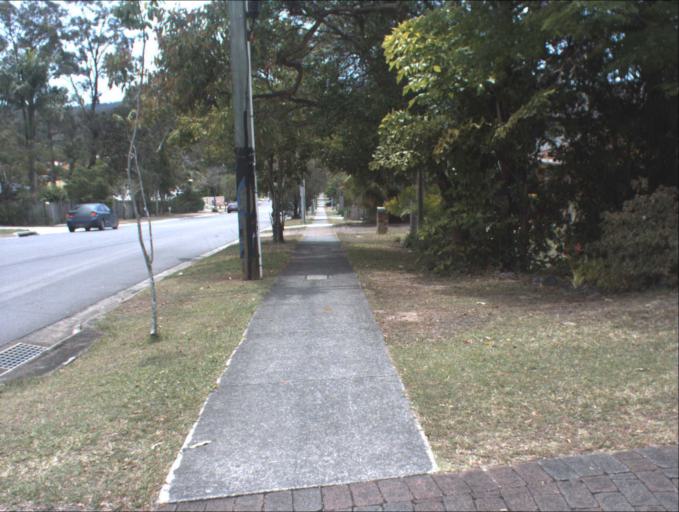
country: AU
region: Queensland
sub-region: Logan
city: Slacks Creek
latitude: -27.6498
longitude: 153.1655
